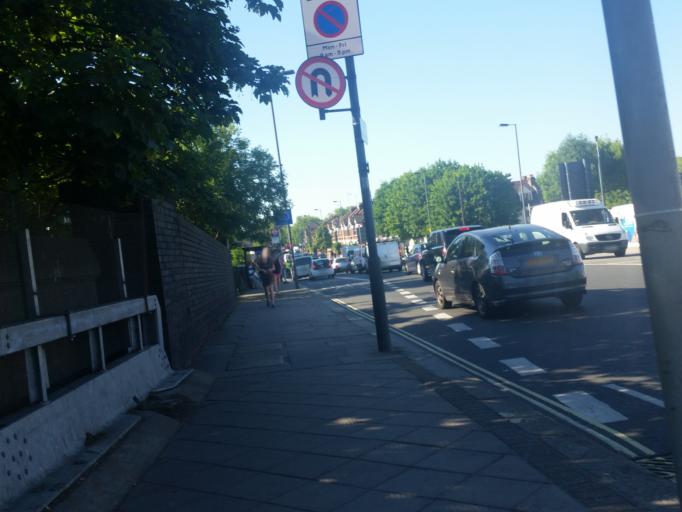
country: GB
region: England
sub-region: Greater London
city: Hammersmith
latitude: 51.5155
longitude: -0.2265
